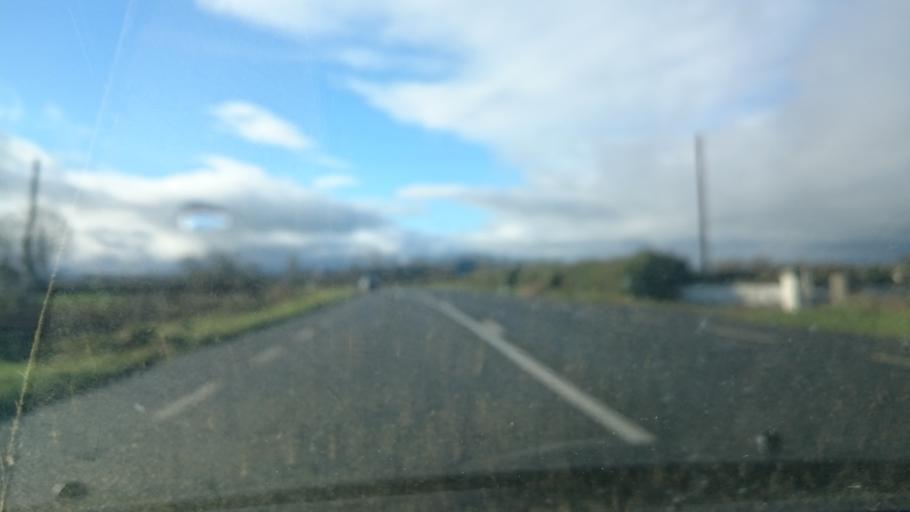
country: IE
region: Leinster
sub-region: Kilkenny
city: Callan
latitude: 52.5721
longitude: -7.3379
